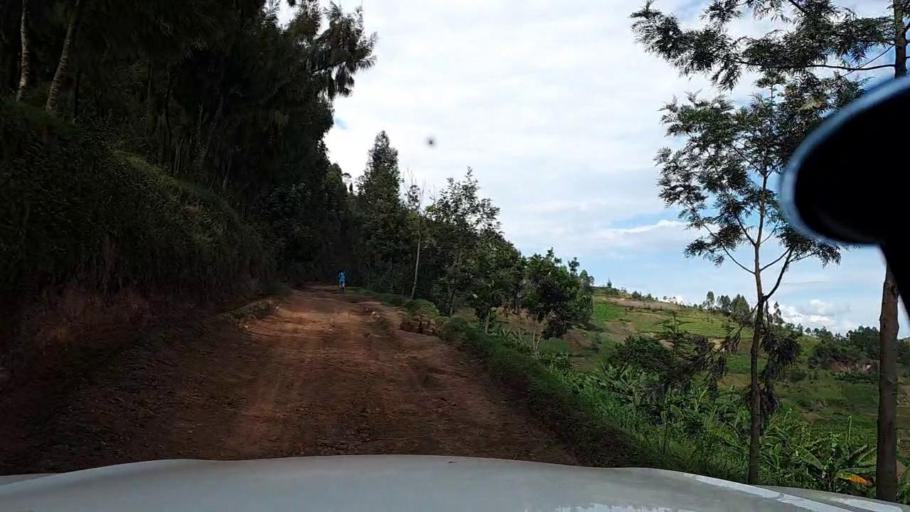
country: RW
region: Kigali
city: Kigali
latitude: -1.7869
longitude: 29.8317
